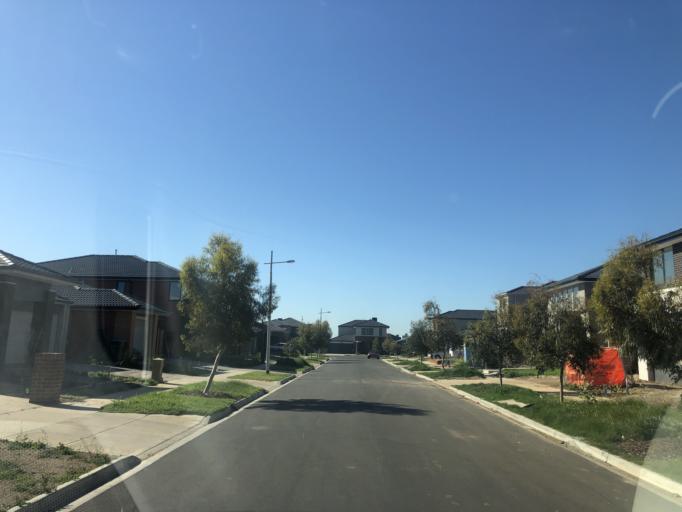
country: AU
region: Victoria
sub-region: Wyndham
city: Point Cook
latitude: -37.9105
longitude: 144.7187
